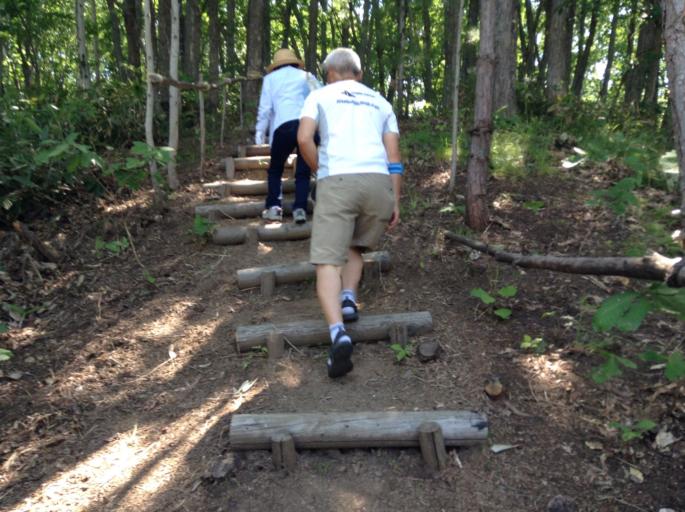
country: JP
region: Hokkaido
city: Nayoro
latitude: 44.2955
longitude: 142.6311
